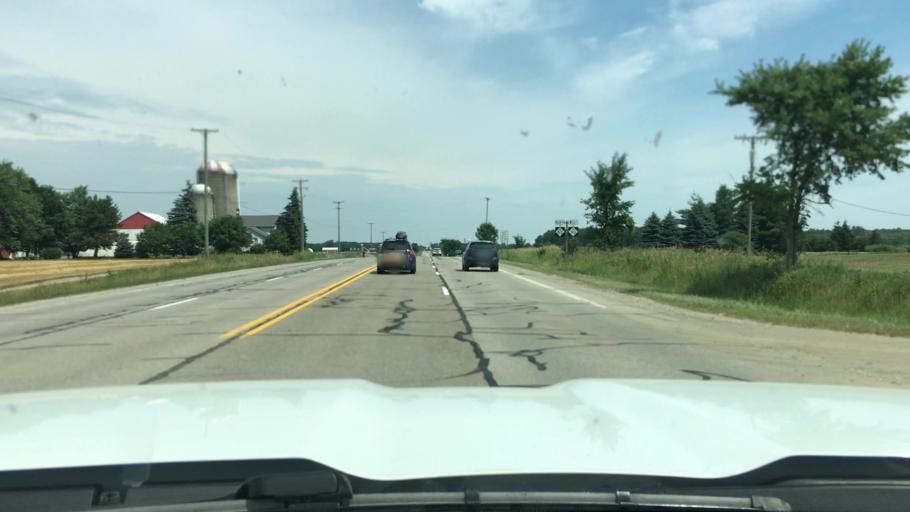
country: US
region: Michigan
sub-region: Sanilac County
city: Brown City
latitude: 43.2251
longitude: -83.0778
